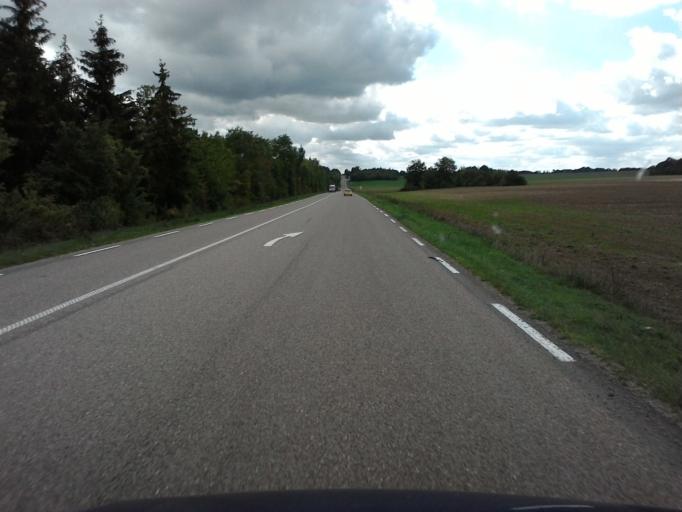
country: FR
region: Lorraine
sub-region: Departement des Vosges
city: Neufchateau
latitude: 48.3952
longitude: 5.7255
